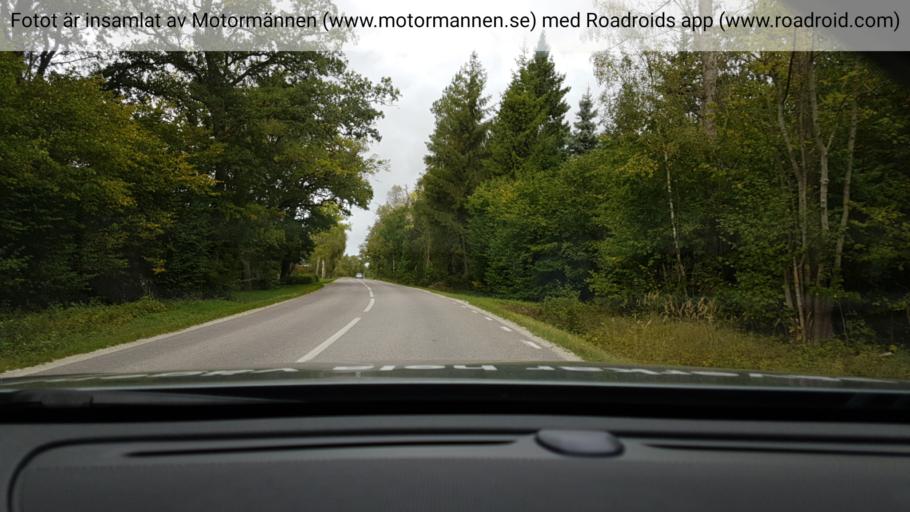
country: SE
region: Gotland
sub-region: Gotland
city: Klintehamn
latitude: 57.4298
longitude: 18.3675
